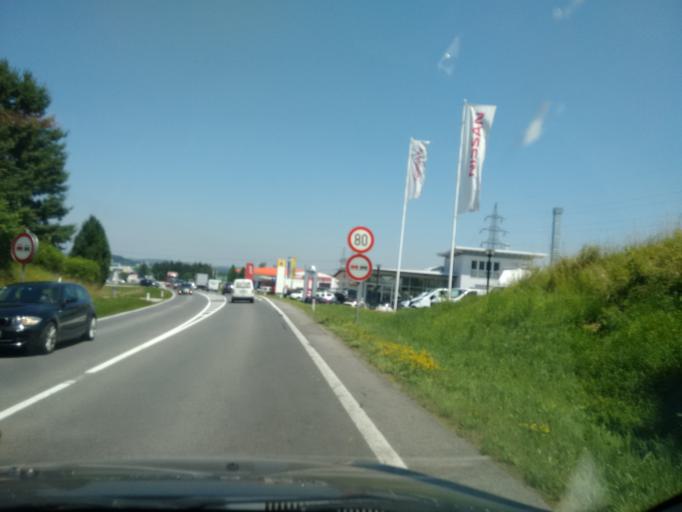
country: AT
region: Upper Austria
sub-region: Politischer Bezirk Gmunden
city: Gmunden
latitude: 47.9225
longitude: 13.7828
